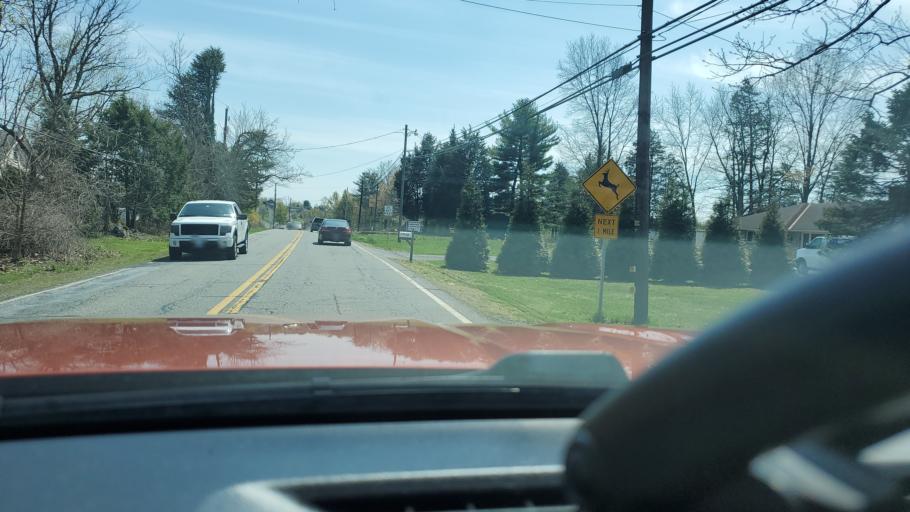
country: US
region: Pennsylvania
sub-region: Montgomery County
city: Red Hill
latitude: 40.3652
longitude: -75.4829
